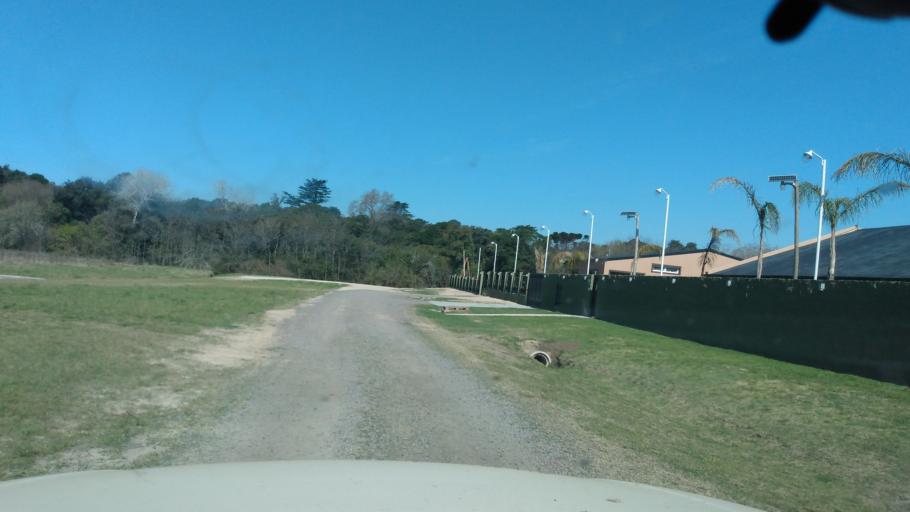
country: AR
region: Buenos Aires
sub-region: Partido de Lujan
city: Lujan
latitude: -34.5761
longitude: -59.1327
